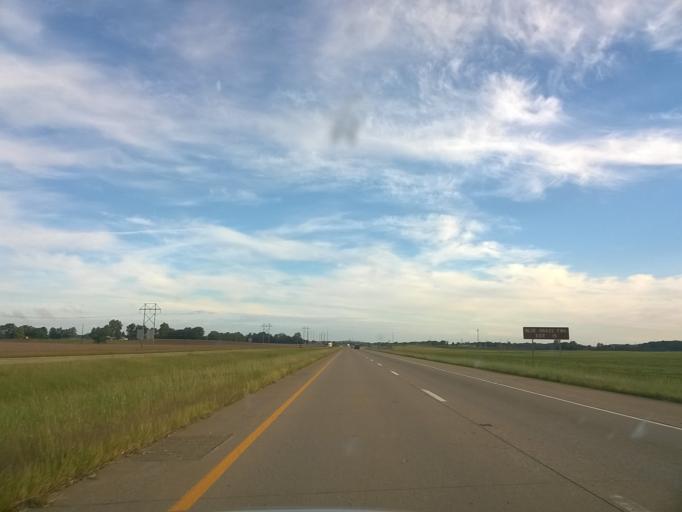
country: US
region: Indiana
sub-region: Vanderburgh County
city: Melody Hill
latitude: 38.0814
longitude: -87.4765
